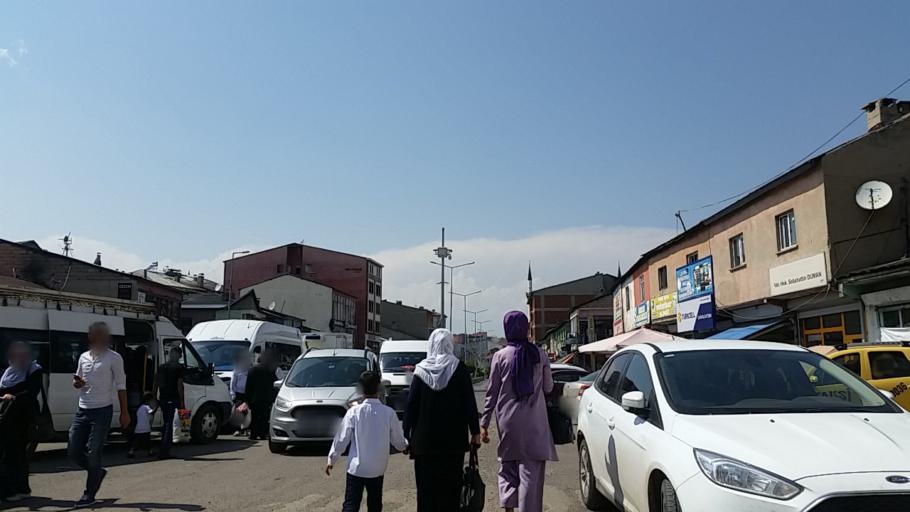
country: TR
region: Agri
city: Agri
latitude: 39.7140
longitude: 43.0537
